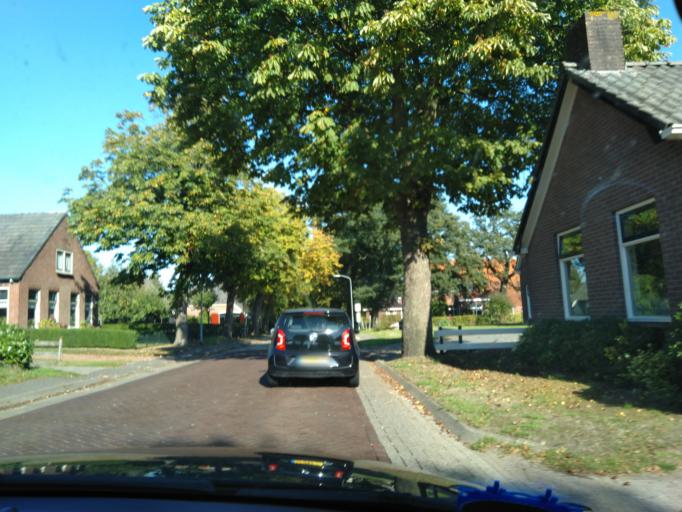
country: NL
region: Drenthe
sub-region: Gemeente Aa en Hunze
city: Anloo
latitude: 53.0530
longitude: 6.7251
